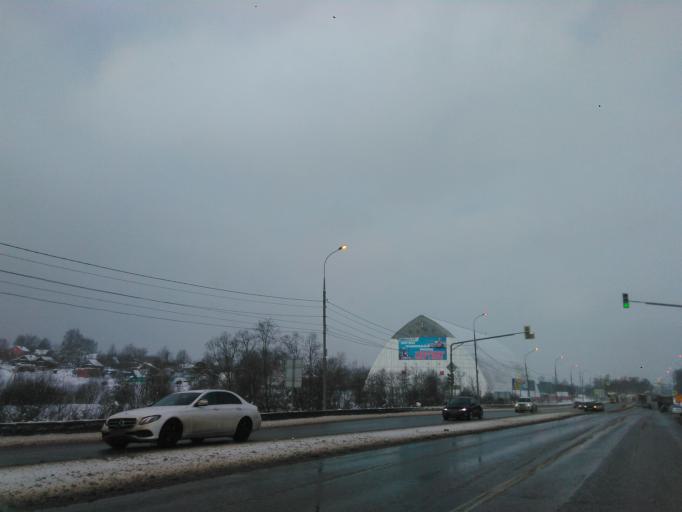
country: RU
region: Moskovskaya
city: Podosinki
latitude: 56.2066
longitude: 37.5228
